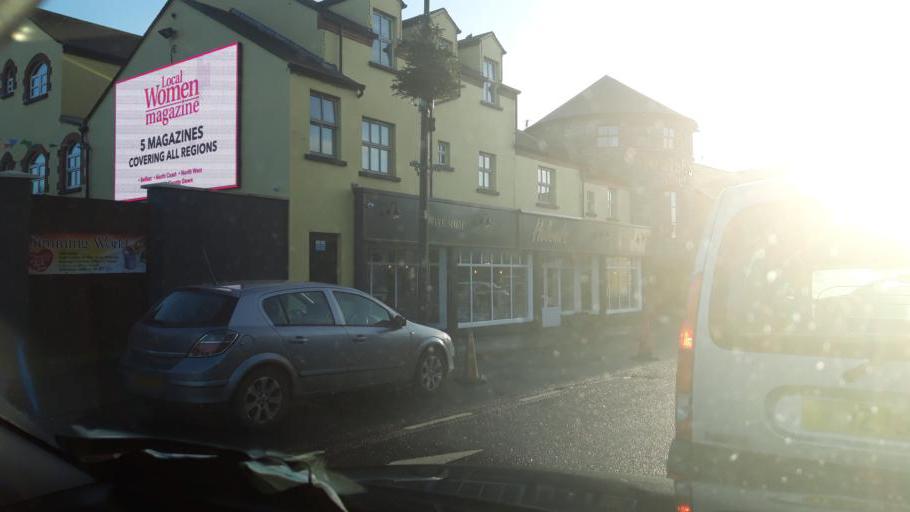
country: GB
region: Northern Ireland
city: Maghera
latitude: 54.8450
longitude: -6.6729
